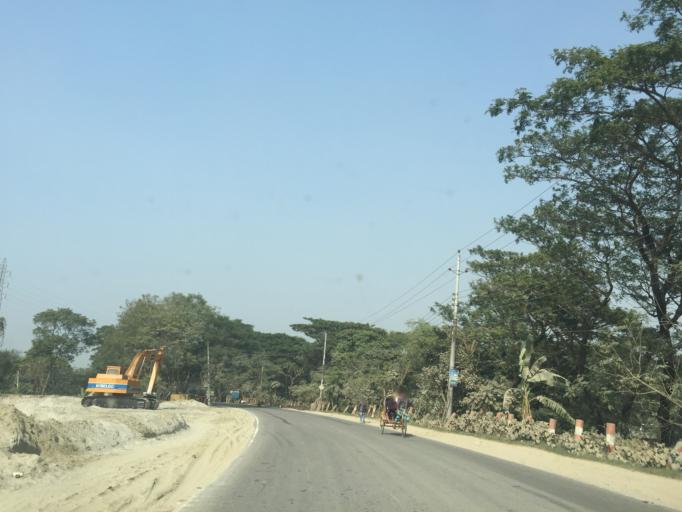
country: BD
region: Dhaka
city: Tungi
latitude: 23.8176
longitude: 90.3418
